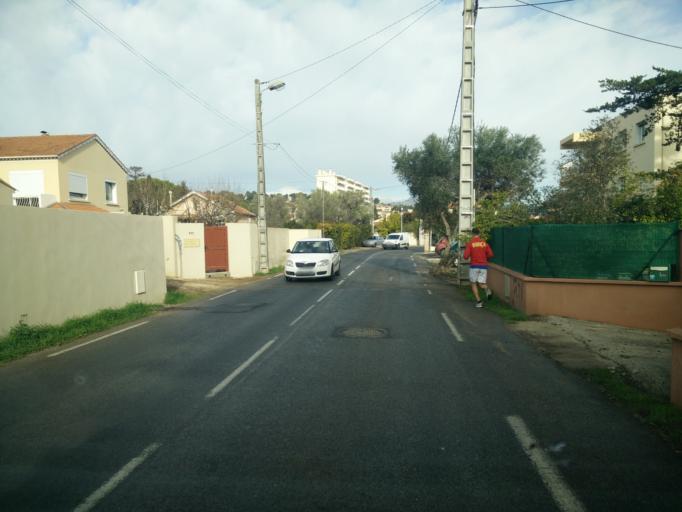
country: FR
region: Provence-Alpes-Cote d'Azur
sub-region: Departement du Var
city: La Seyne-sur-Mer
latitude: 43.0796
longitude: 5.8769
